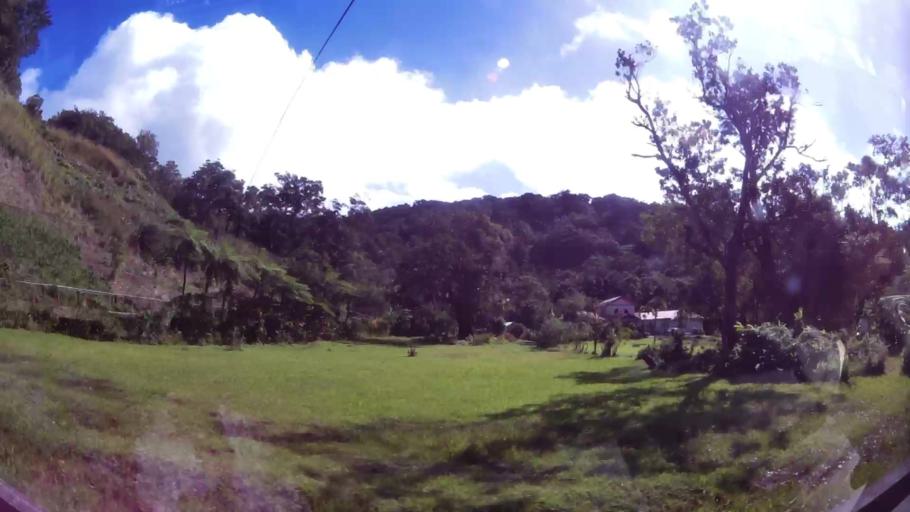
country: DM
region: Saint Paul
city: Pont Casse
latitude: 15.3611
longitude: -61.3545
